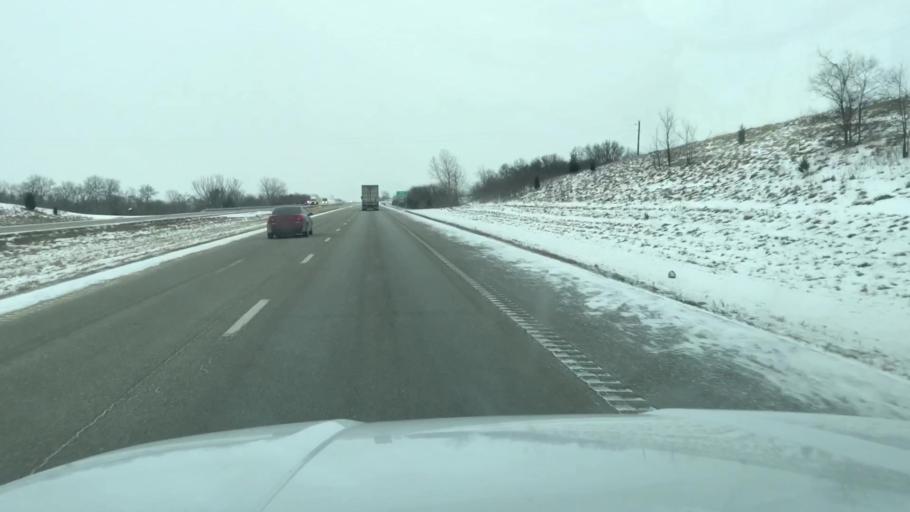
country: US
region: Missouri
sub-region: Buchanan County
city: Saint Joseph
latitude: 39.7476
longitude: -94.7054
